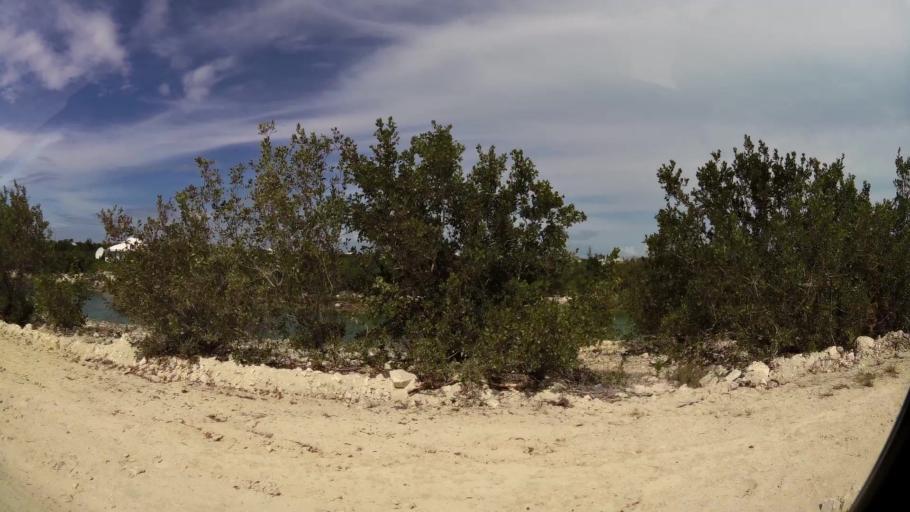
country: BS
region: Mayaguana
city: Abraham's Bay
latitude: 21.7719
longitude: -72.2401
